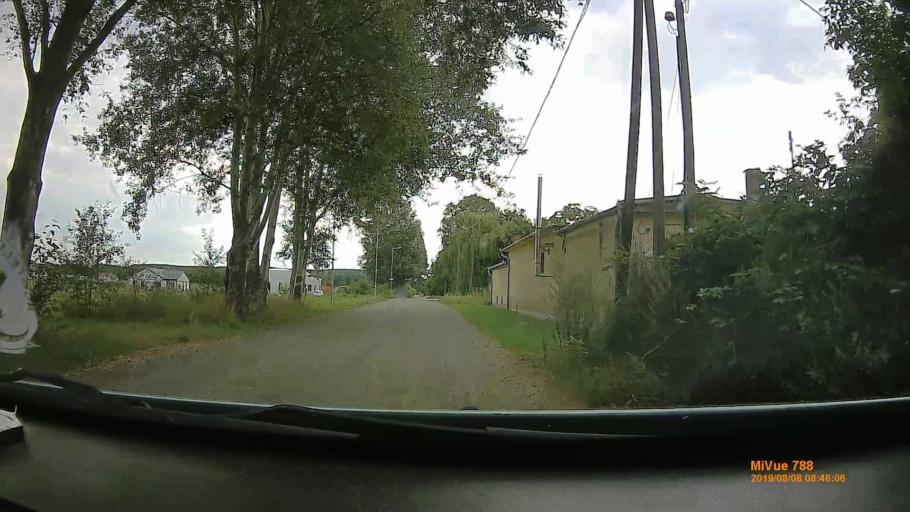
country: HU
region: Hajdu-Bihar
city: Debrecen
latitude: 47.5963
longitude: 21.6377
